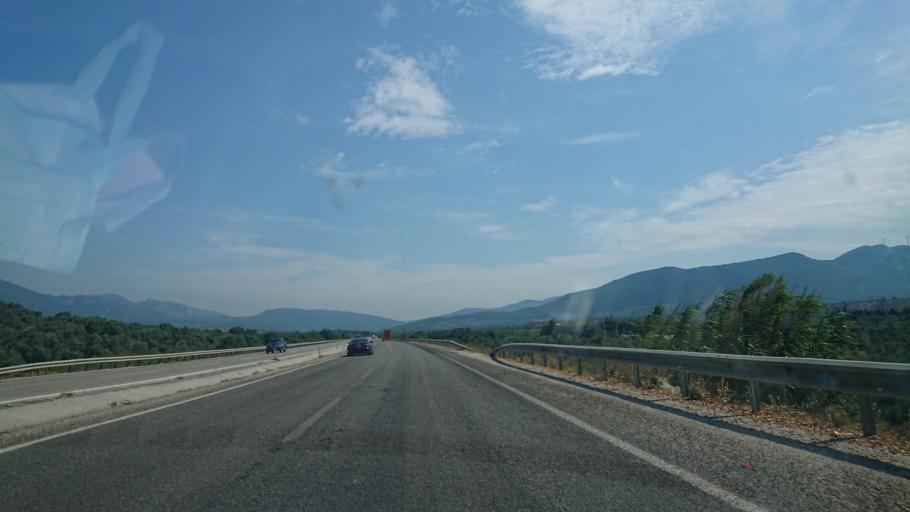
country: TR
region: Izmir
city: Dagkizilca
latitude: 38.2711
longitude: 27.3956
